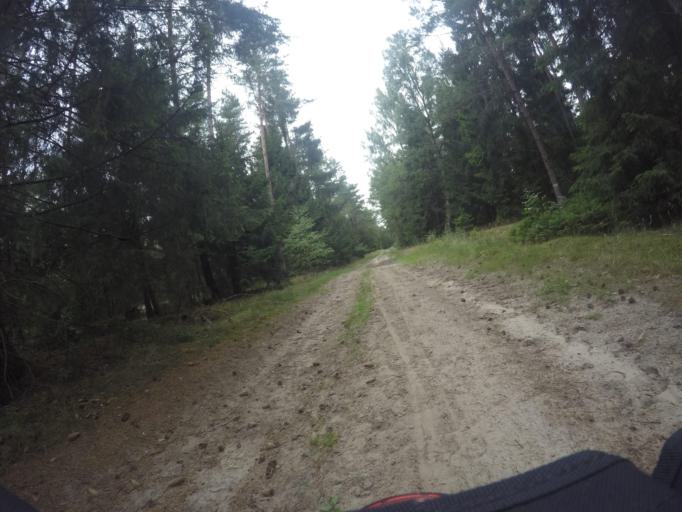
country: DE
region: Lower Saxony
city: Thomasburg
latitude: 53.2355
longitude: 10.6918
